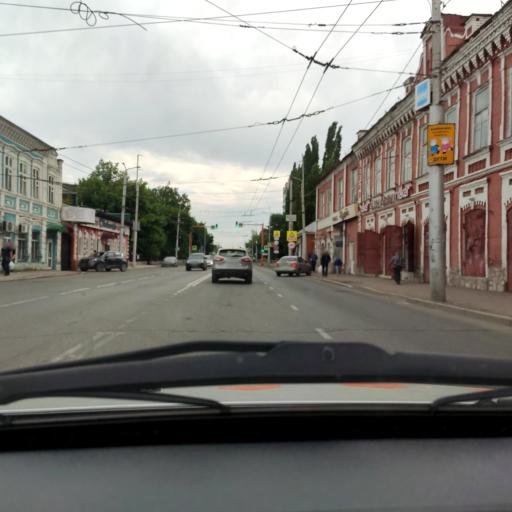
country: RU
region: Bashkortostan
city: Sterlitamak
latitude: 53.6191
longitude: 55.9608
